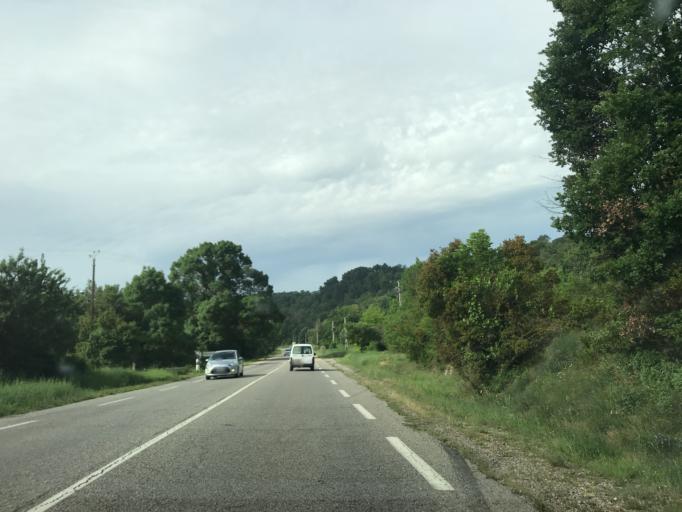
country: FR
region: Provence-Alpes-Cote d'Azur
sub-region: Departement du Var
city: Rians
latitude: 43.6213
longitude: 5.7660
